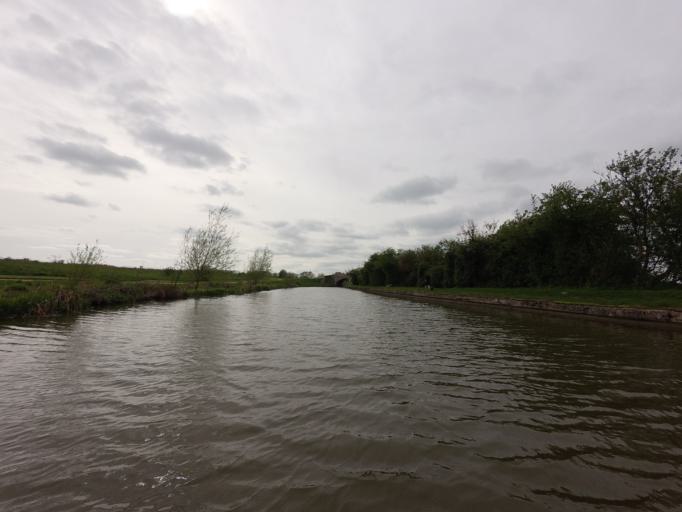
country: GB
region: England
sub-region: Milton Keynes
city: Bradwell
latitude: 52.0740
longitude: -0.7771
